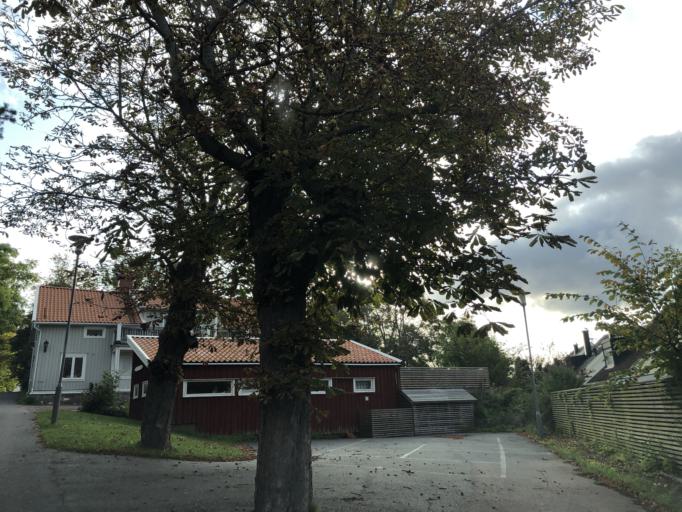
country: SE
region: Vaestra Goetaland
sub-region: Goteborg
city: Majorna
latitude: 57.6651
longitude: 11.8784
